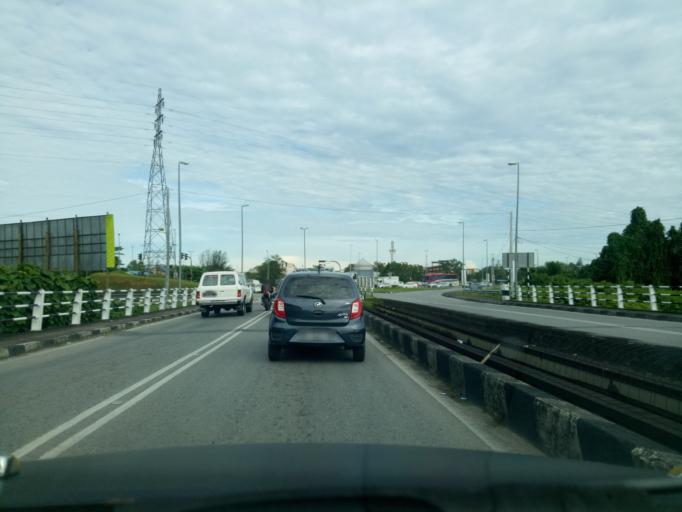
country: MY
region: Sarawak
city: Kuching
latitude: 1.4478
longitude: 110.3292
